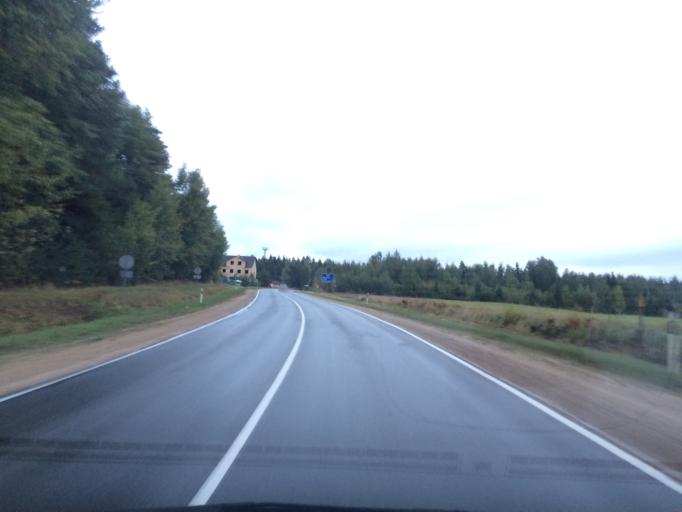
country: LV
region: Salas
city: Sala
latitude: 56.5465
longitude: 25.8023
